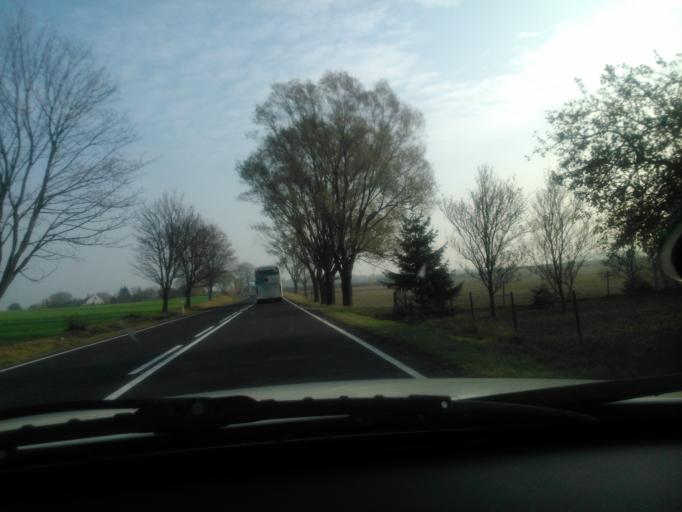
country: PL
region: Kujawsko-Pomorskie
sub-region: Powiat brodnicki
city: Bobrowo
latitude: 53.2346
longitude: 19.2725
